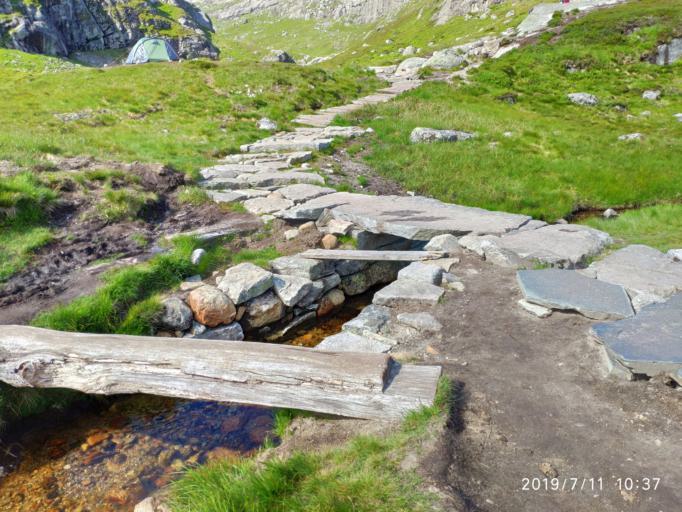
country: NO
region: Vest-Agder
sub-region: Sirdal
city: Tonstad
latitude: 59.0408
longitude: 6.6417
